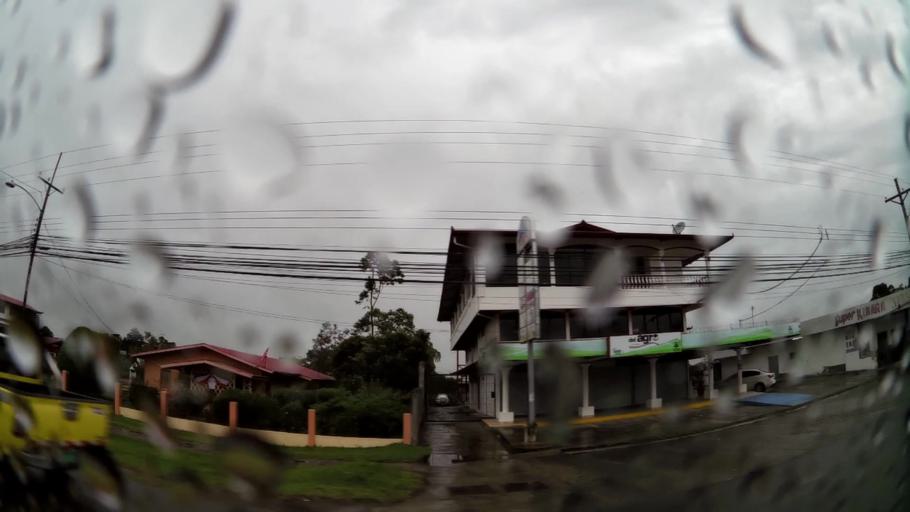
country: PA
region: Chiriqui
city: Volcan
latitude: 8.7803
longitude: -82.6456
